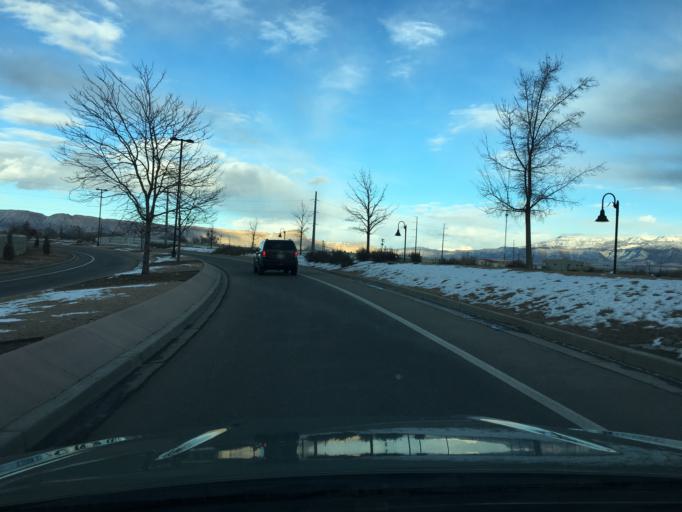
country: US
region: Colorado
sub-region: Mesa County
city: Grand Junction
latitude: 39.0563
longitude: -108.5477
